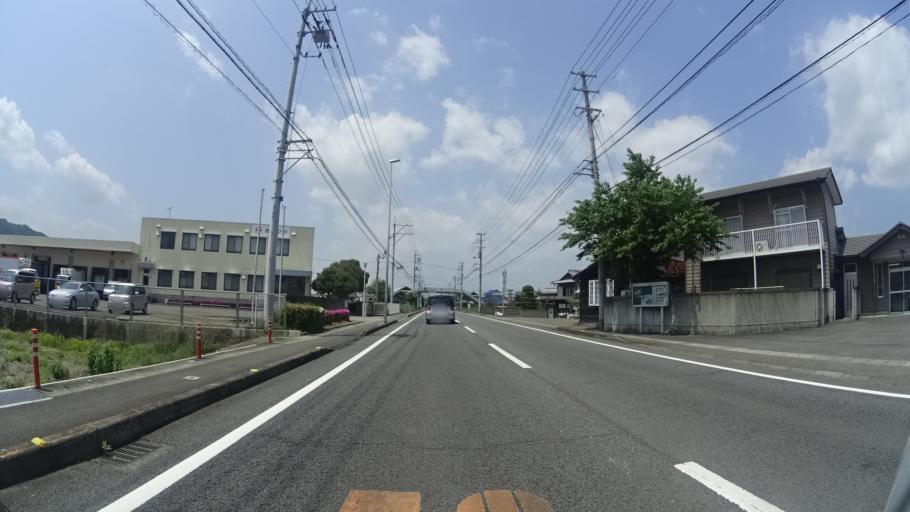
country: JP
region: Tokushima
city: Ishii
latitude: 34.0680
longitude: 134.4142
